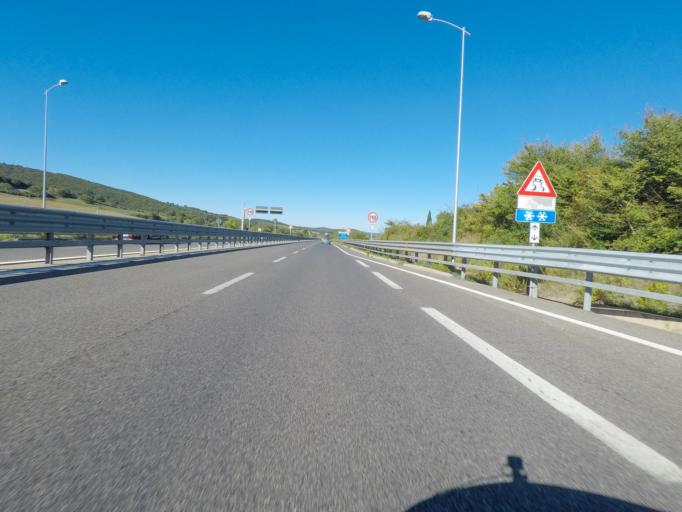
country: IT
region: Tuscany
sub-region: Provincia di Grosseto
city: Campagnatico
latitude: 42.8925
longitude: 11.2375
